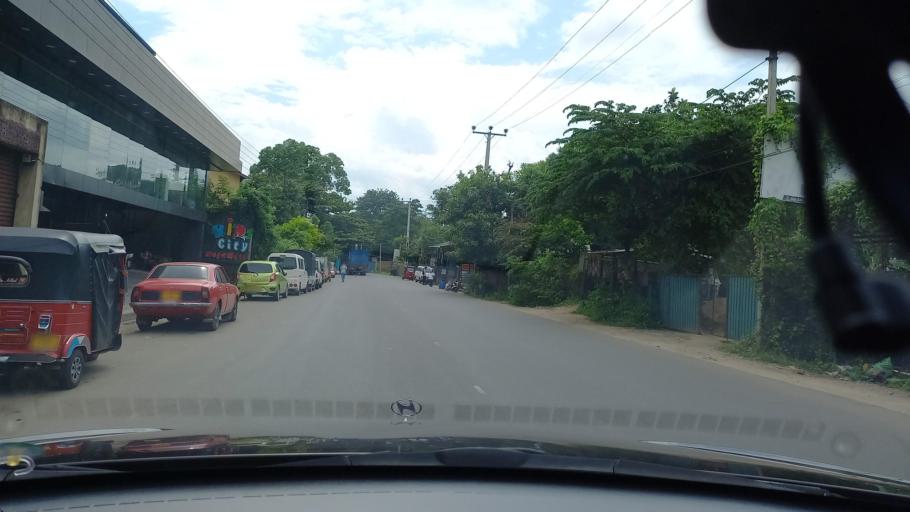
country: LK
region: Central
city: Kadugannawa
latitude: 7.2487
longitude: 80.4640
